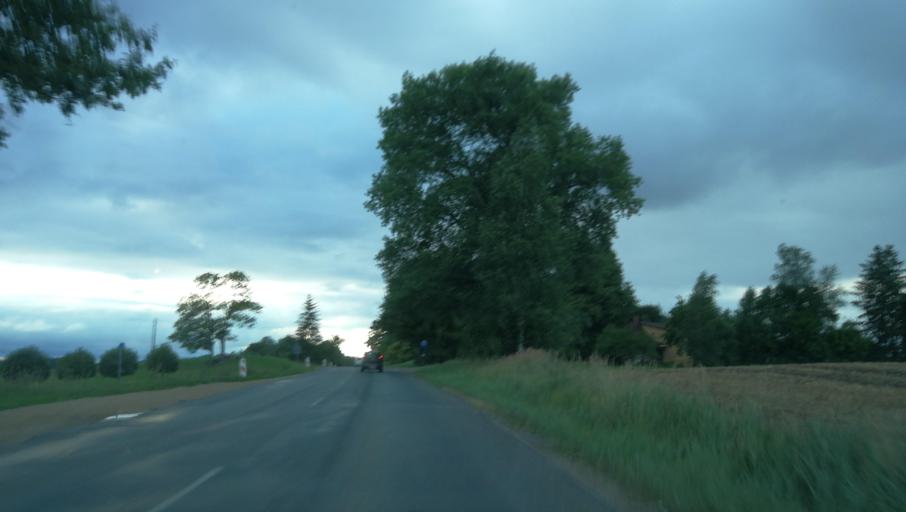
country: LV
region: Malpils
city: Malpils
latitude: 57.0204
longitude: 24.8498
